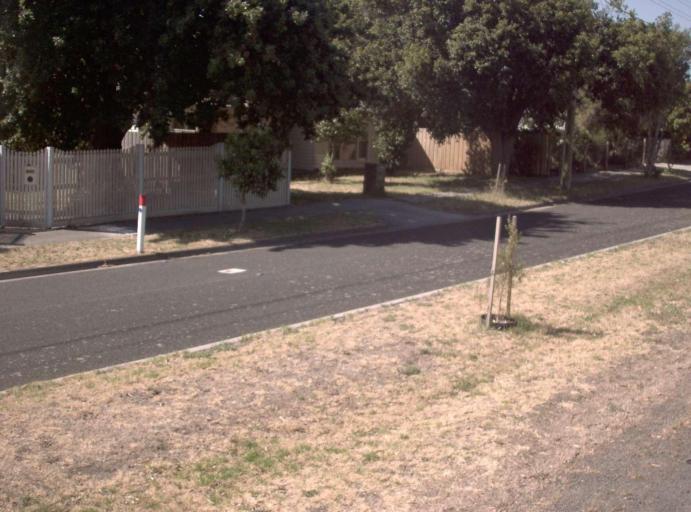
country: AU
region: Victoria
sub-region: Frankston
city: Frankston North
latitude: -38.1238
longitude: 145.1408
